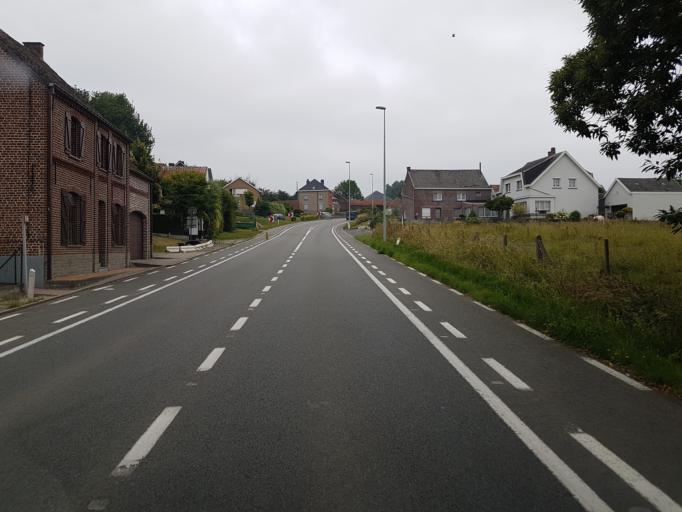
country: BE
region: Flanders
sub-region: Provincie Oost-Vlaanderen
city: Haaltert
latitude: 50.8503
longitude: 3.9585
